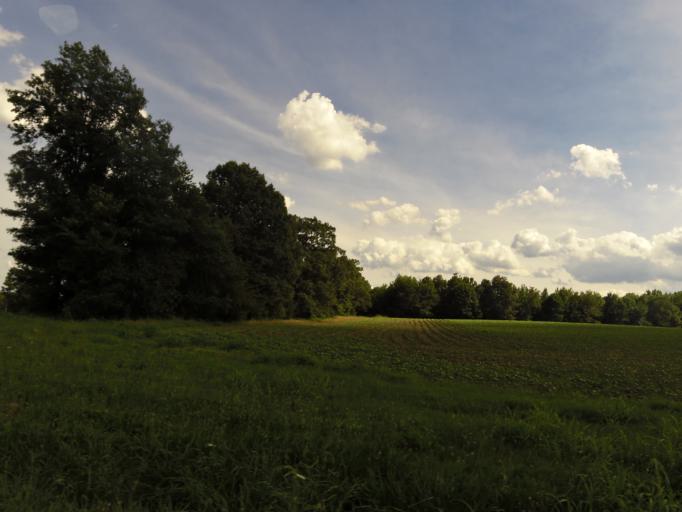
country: US
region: Tennessee
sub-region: Gibson County
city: Milan
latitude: 35.9850
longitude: -88.6064
